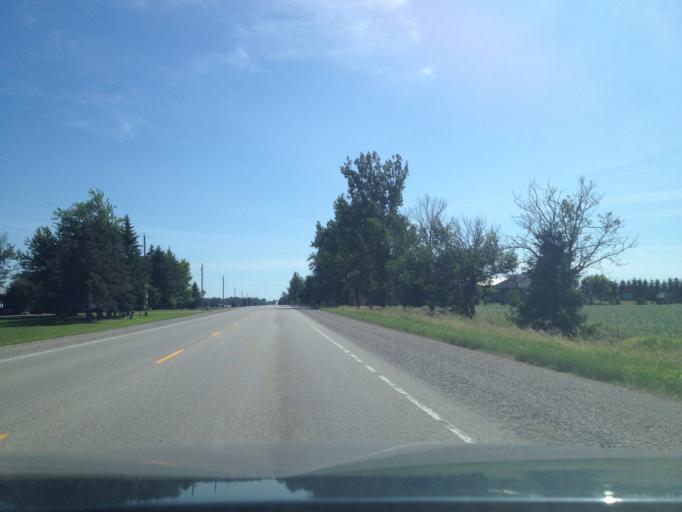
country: CA
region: Ontario
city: Stratford
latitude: 43.4897
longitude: -80.8867
